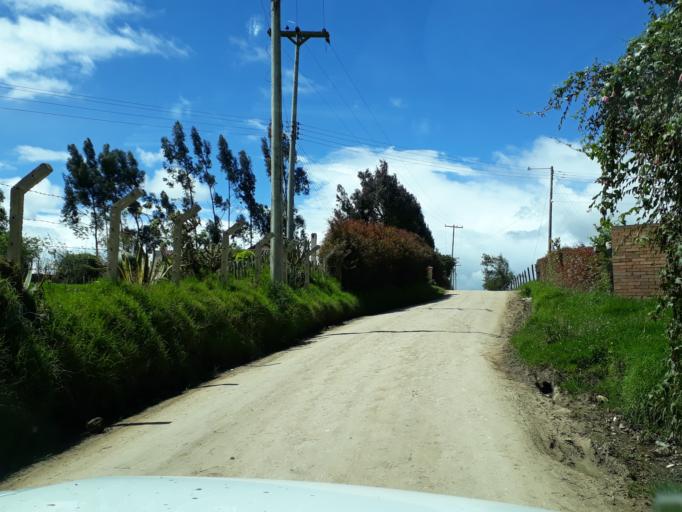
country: CO
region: Cundinamarca
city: Guasca
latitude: 4.8536
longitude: -73.8802
